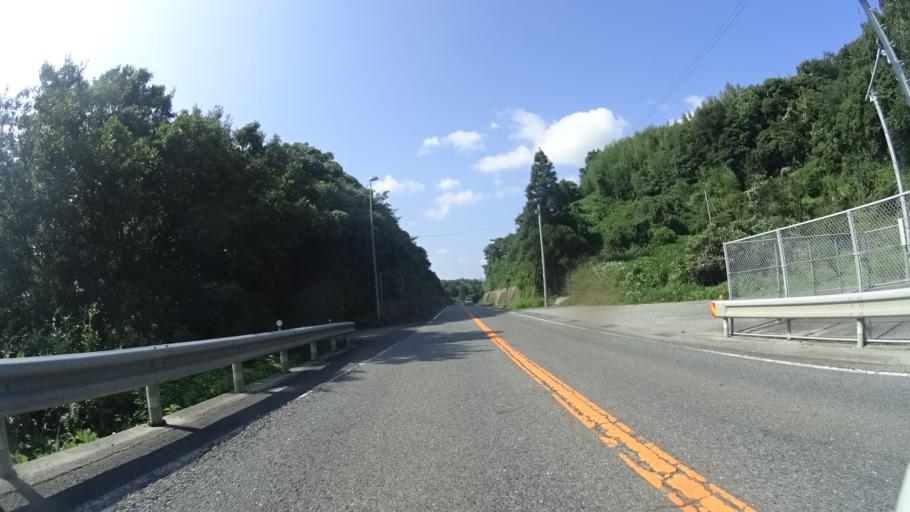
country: JP
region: Shimane
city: Gotsucho
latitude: 35.0588
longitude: 132.3168
